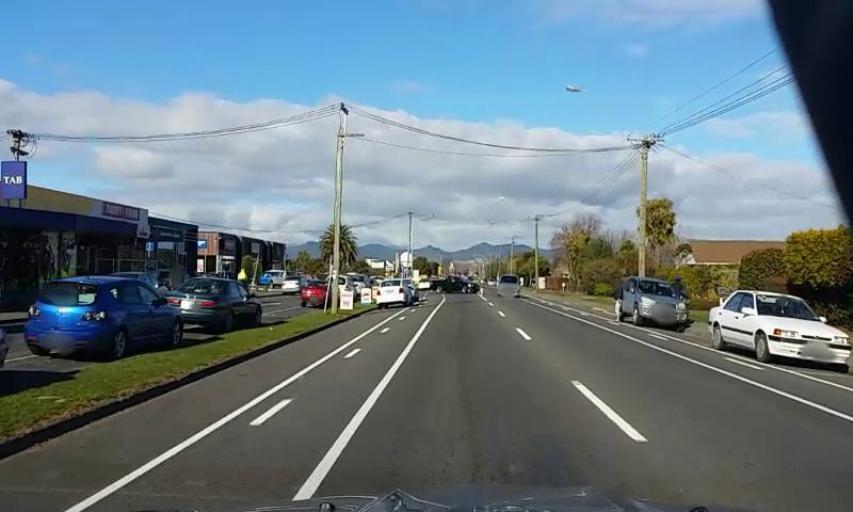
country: NZ
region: Canterbury
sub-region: Christchurch City
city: Christchurch
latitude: -43.4987
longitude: 172.6619
